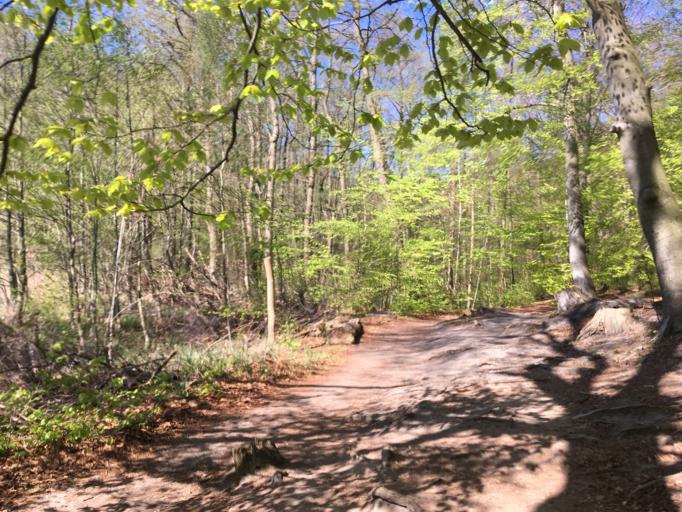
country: DE
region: Brandenburg
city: Wandlitz
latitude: 52.7508
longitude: 13.5109
